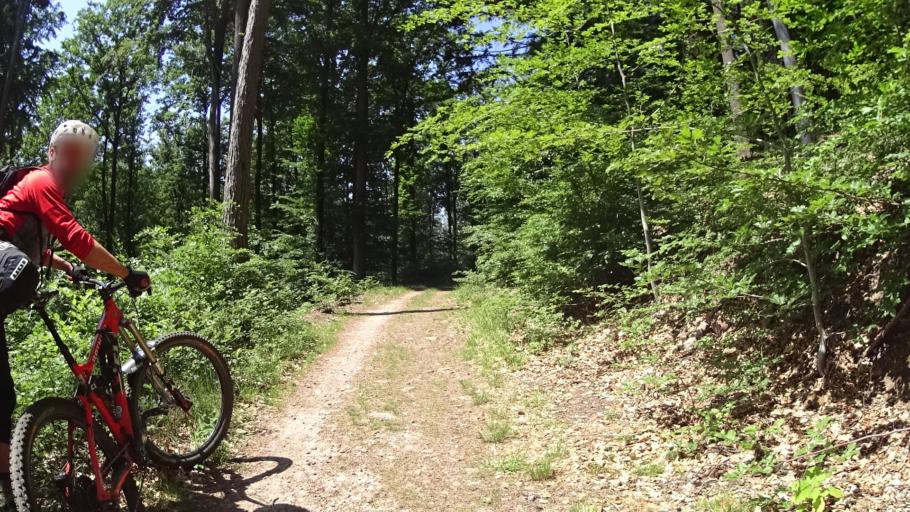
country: DE
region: Baden-Wuerttemberg
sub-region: Karlsruhe Region
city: Neckargemund
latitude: 49.4019
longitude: 8.7868
